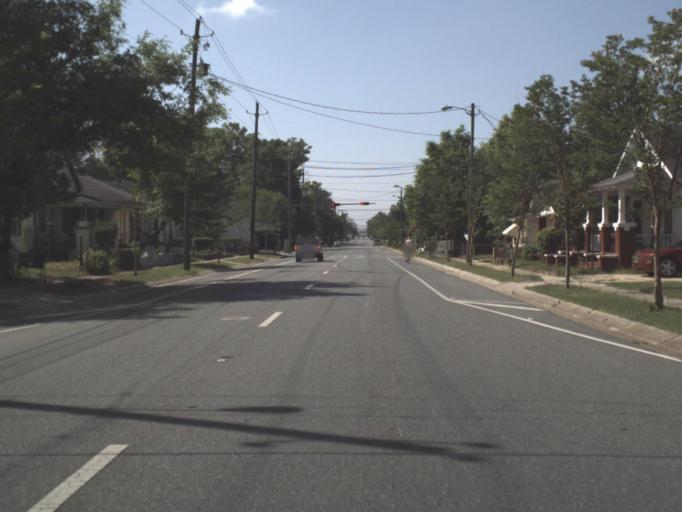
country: US
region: Florida
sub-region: Escambia County
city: Pensacola
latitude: 30.4299
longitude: -87.2136
